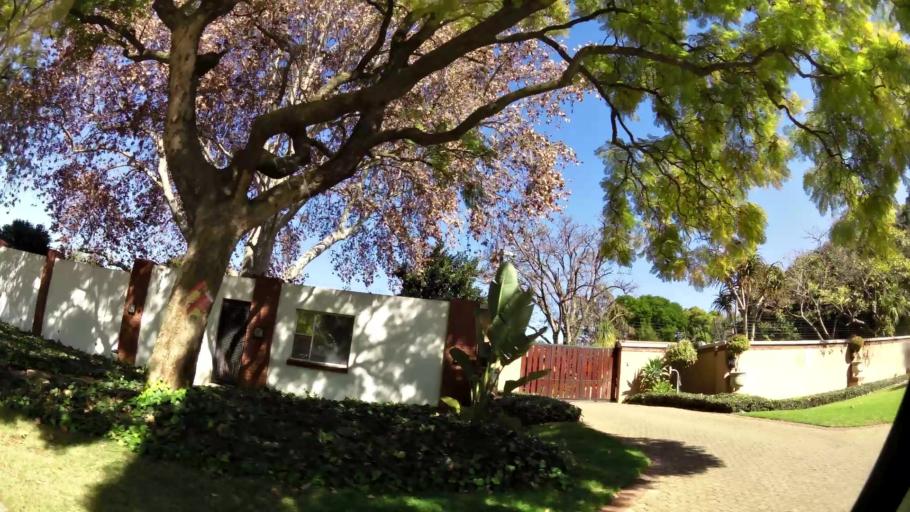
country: ZA
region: Gauteng
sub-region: City of Tshwane Metropolitan Municipality
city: Pretoria
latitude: -25.7674
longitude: 28.2440
